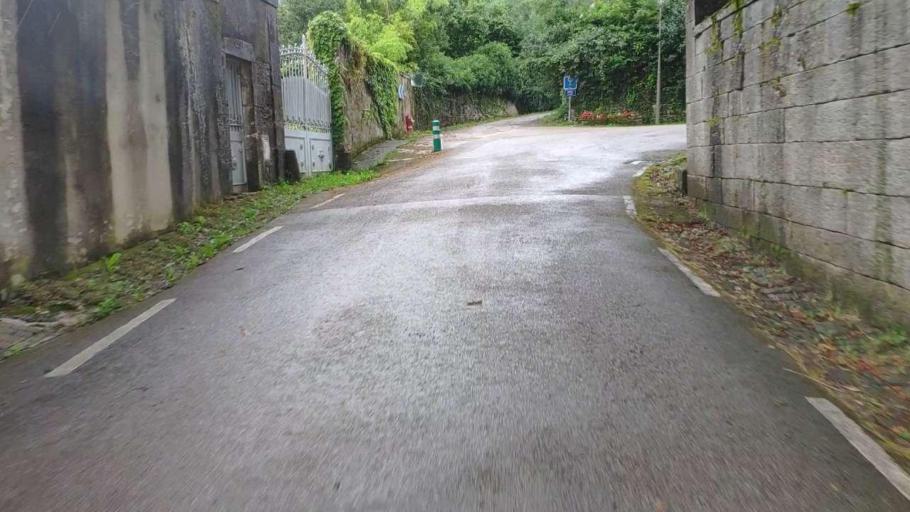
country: FR
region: Franche-Comte
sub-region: Departement du Jura
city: Poligny
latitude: 46.7883
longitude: 5.6171
